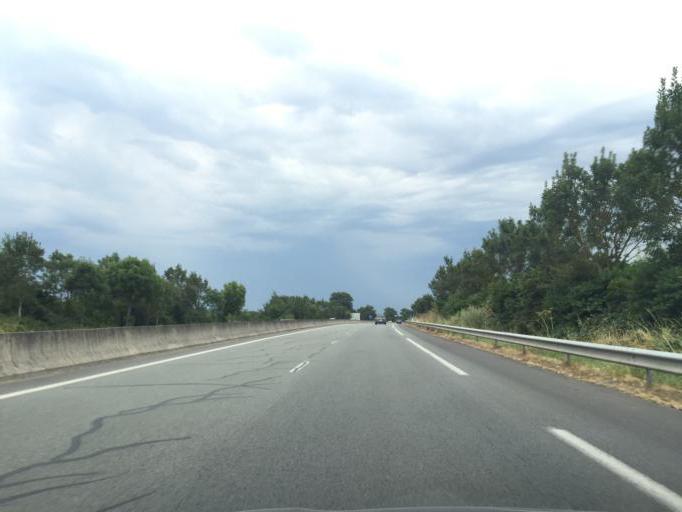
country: FR
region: Auvergne
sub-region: Departement de l'Allier
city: Toulon-sur-Allier
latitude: 46.5140
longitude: 3.3555
